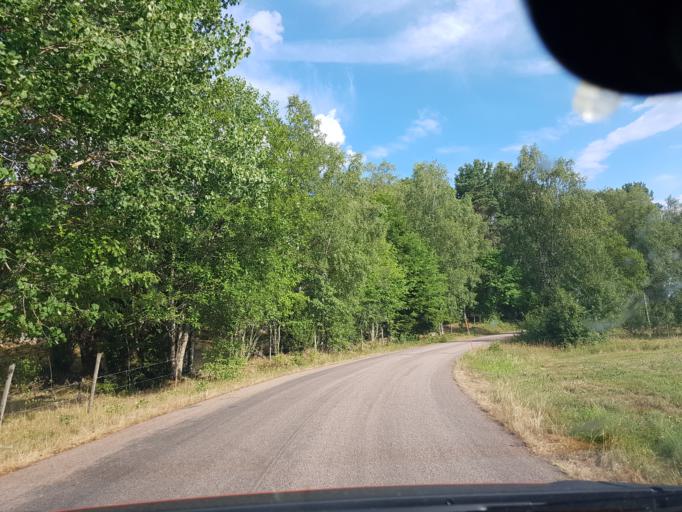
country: SE
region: Joenkoeping
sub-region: Gislaveds Kommun
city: Reftele
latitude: 57.2085
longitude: 13.5904
